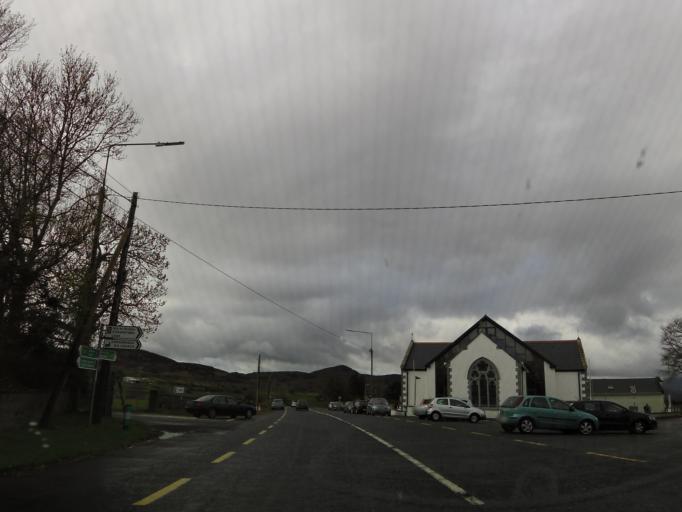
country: IE
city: Ballisodare
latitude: 54.2084
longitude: -8.5331
